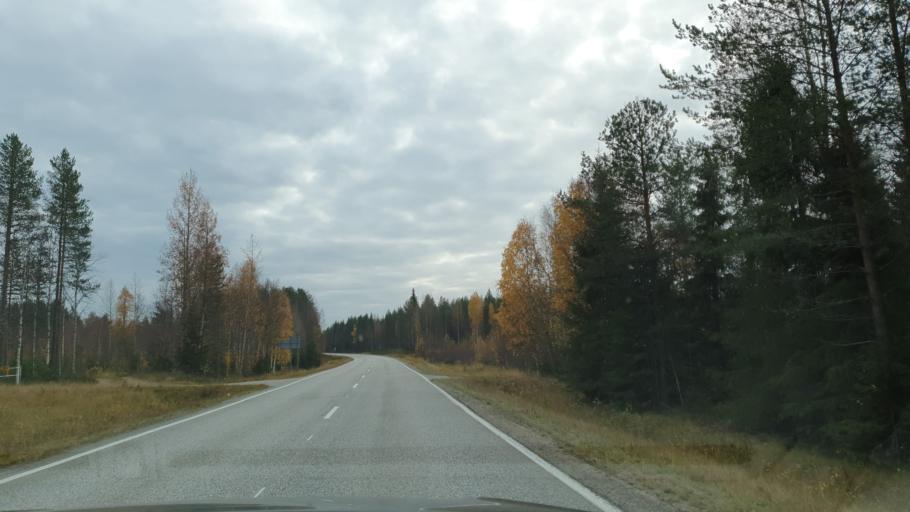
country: FI
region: Kainuu
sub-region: Kehys-Kainuu
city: Puolanka
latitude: 65.2446
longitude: 27.5806
